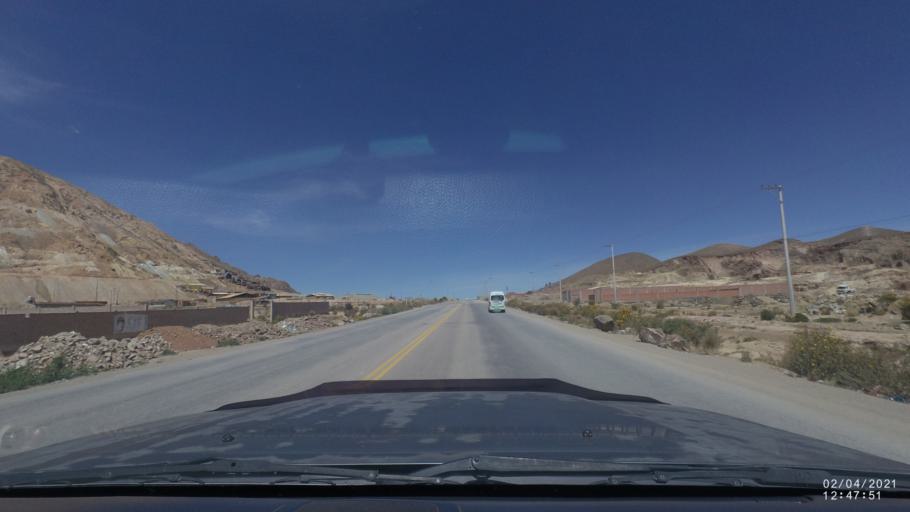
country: BO
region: Oruro
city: Oruro
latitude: -17.9577
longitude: -67.1430
